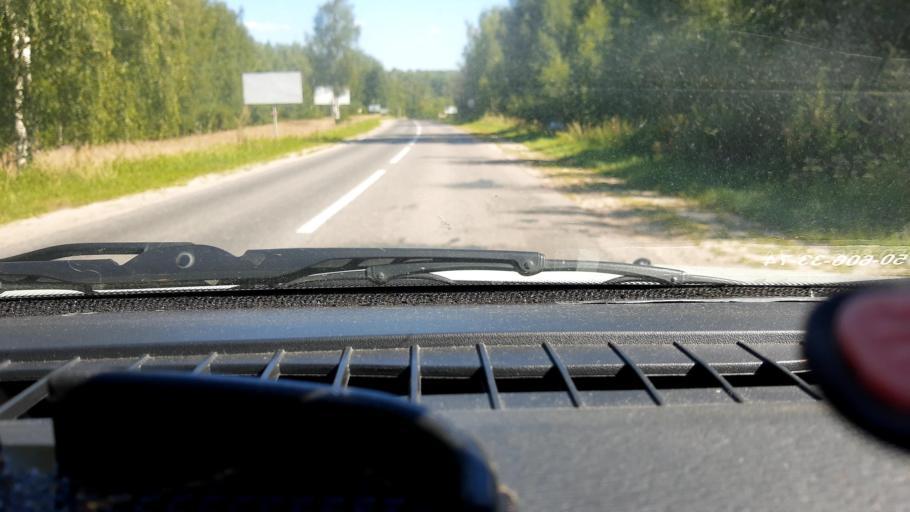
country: RU
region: Nizjnij Novgorod
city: Zavolzh'ye
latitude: 56.6900
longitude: 43.4246
